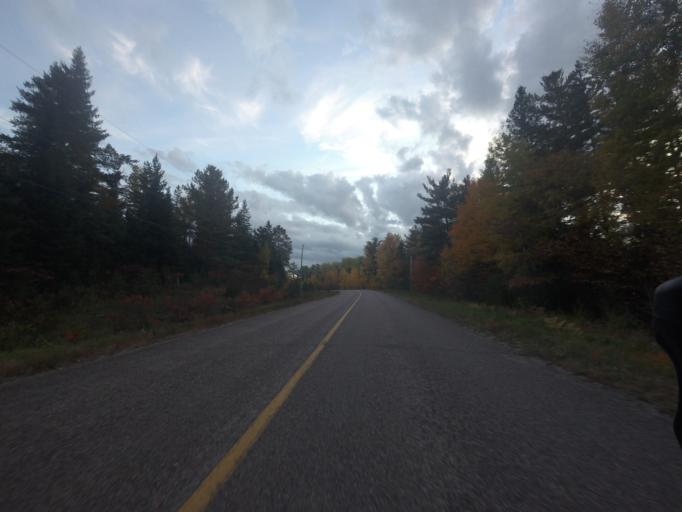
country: CA
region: Ontario
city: Renfrew
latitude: 45.3872
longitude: -76.9546
